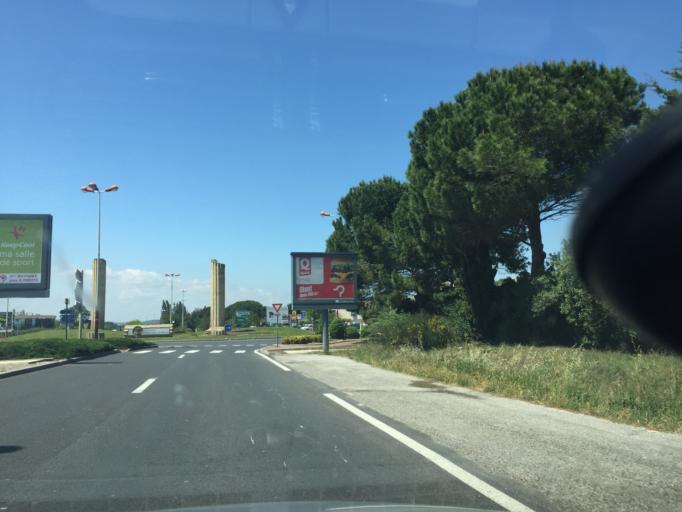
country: FR
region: Languedoc-Roussillon
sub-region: Departement de l'Aude
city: Narbonne
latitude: 43.1816
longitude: 3.0306
